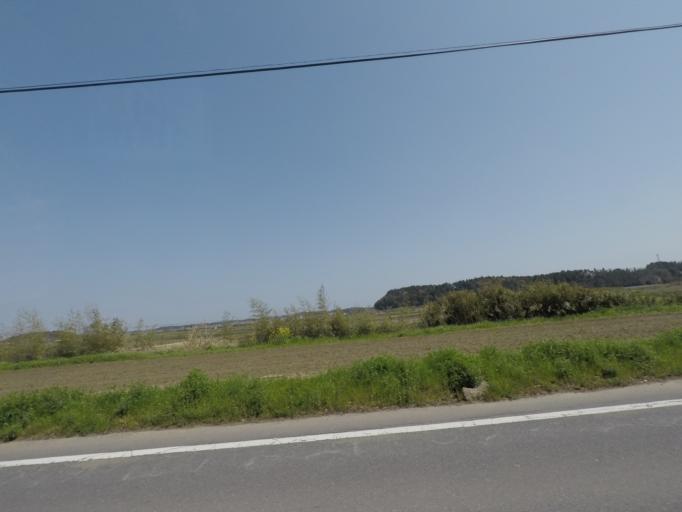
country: JP
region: Chiba
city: Yokaichiba
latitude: 35.6966
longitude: 140.4611
